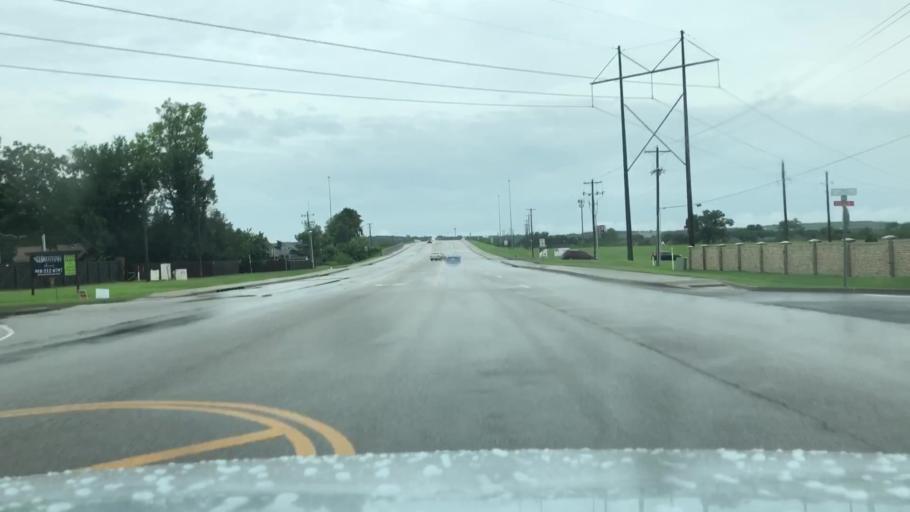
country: US
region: Oklahoma
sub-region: Tulsa County
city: Jenks
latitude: 36.0030
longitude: -96.0065
